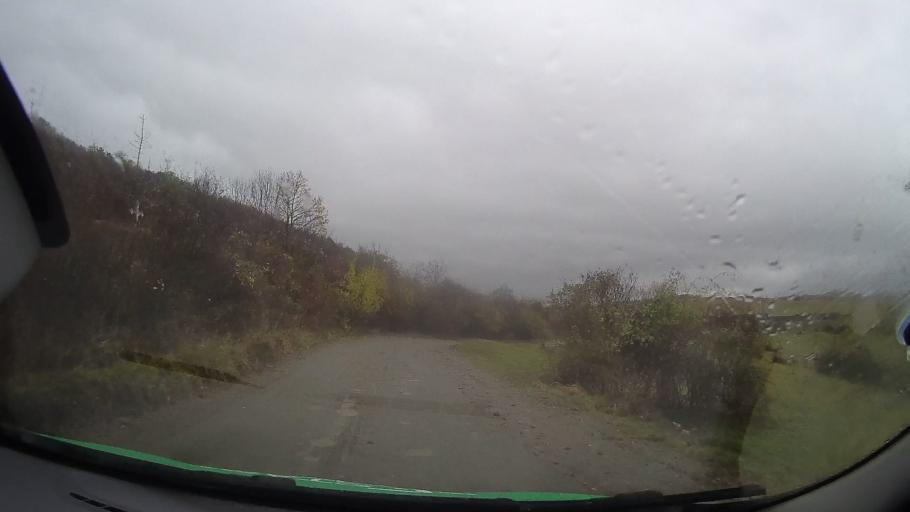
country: RO
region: Mures
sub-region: Comuna Vatava
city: Vatava
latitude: 46.9524
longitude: 24.7342
